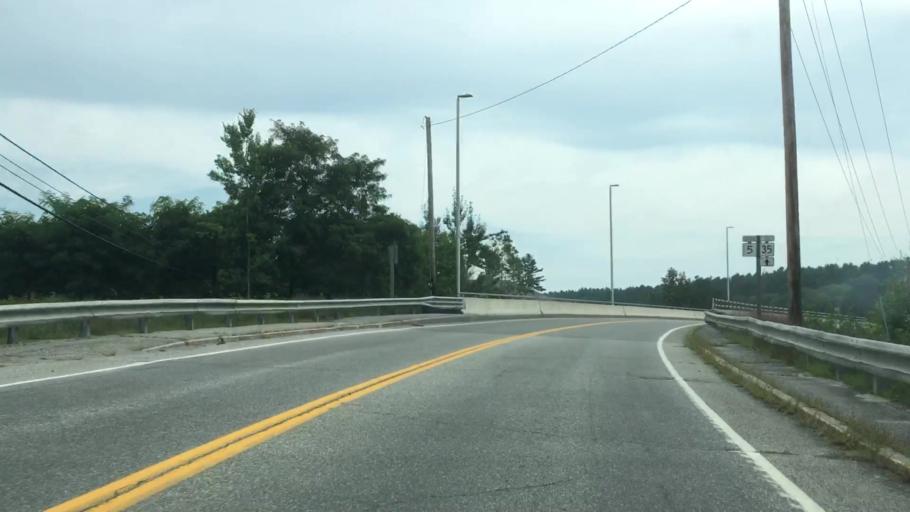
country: US
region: Maine
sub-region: Oxford County
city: Bethel
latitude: 44.4109
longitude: -70.7951
